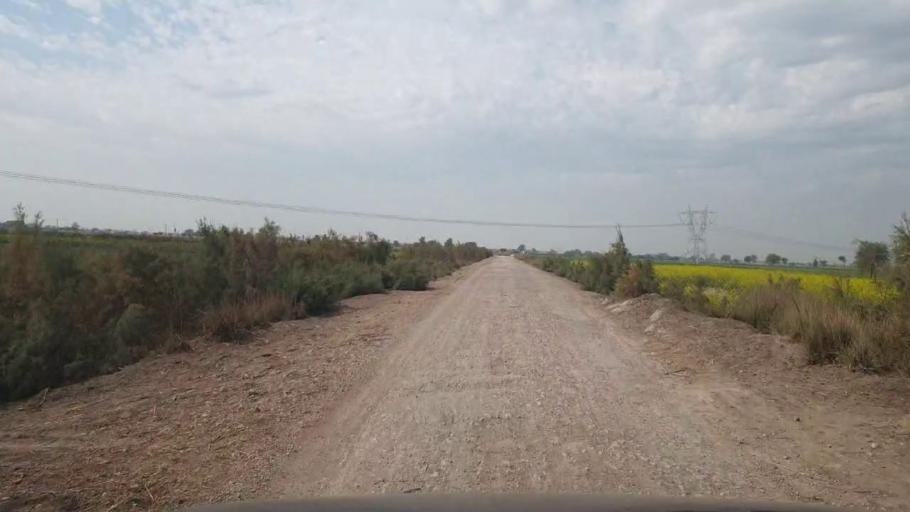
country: PK
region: Sindh
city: Sakrand
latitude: 26.0141
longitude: 68.3876
